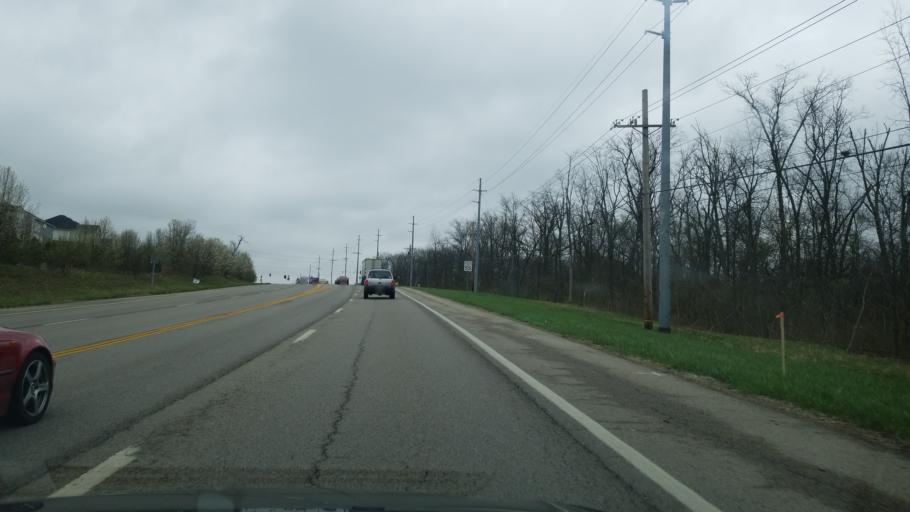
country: US
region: Ohio
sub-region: Butler County
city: Beckett Ridge
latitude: 39.3704
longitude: -84.4555
